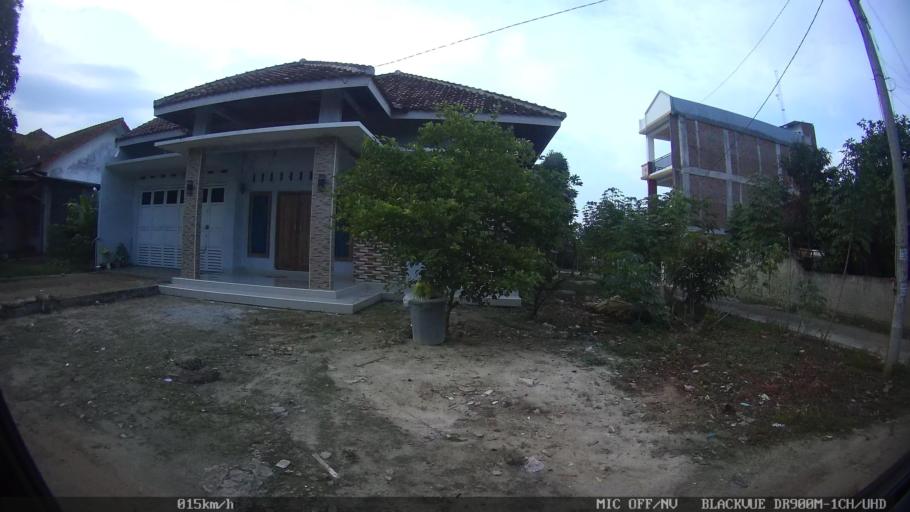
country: ID
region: Lampung
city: Kedaton
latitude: -5.3814
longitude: 105.2317
